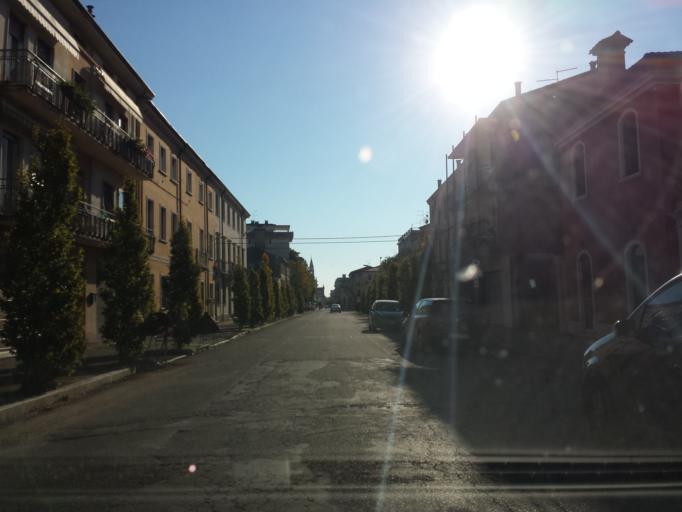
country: IT
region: Veneto
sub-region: Provincia di Verona
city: San Bonifacio
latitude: 45.4017
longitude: 11.2740
